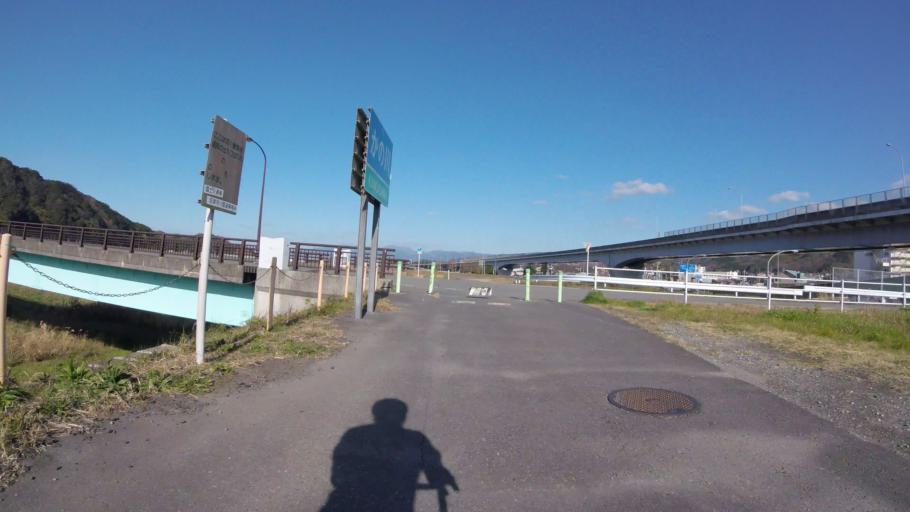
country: JP
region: Shizuoka
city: Mishima
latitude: 35.0099
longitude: 138.9392
